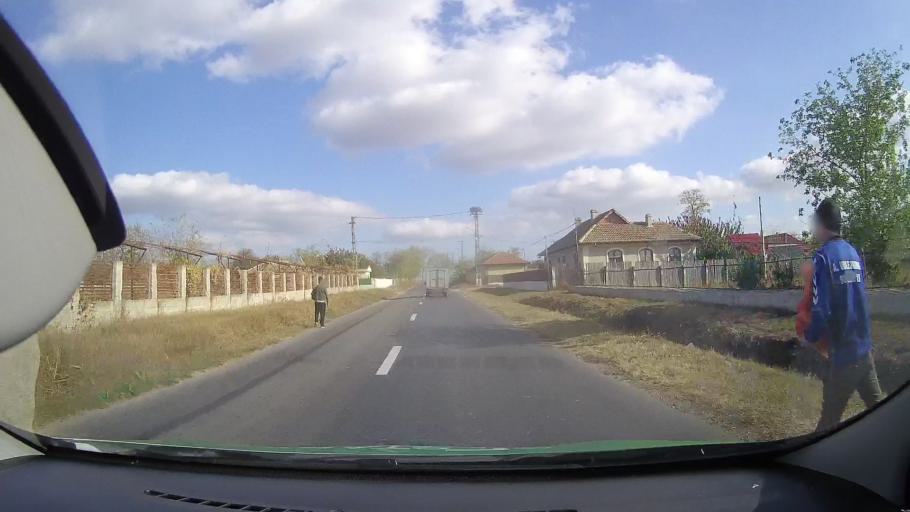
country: RO
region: Constanta
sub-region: Comuna Cogealac
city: Tariverde
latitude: 44.5634
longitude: 28.6019
